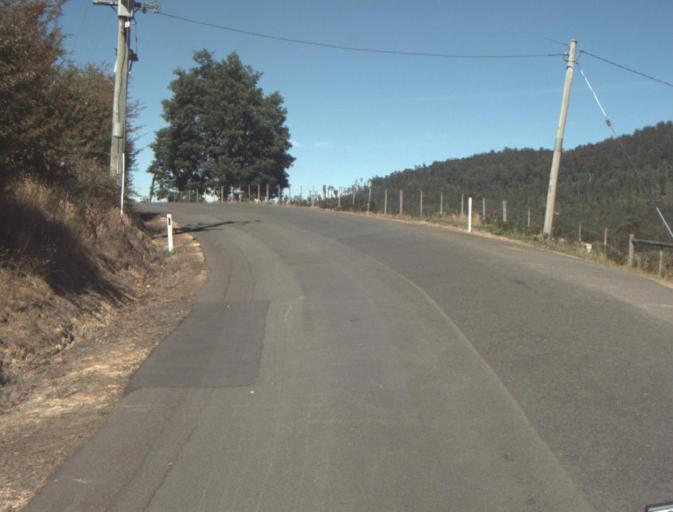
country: AU
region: Tasmania
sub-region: Launceston
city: Newstead
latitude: -41.3500
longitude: 147.3035
